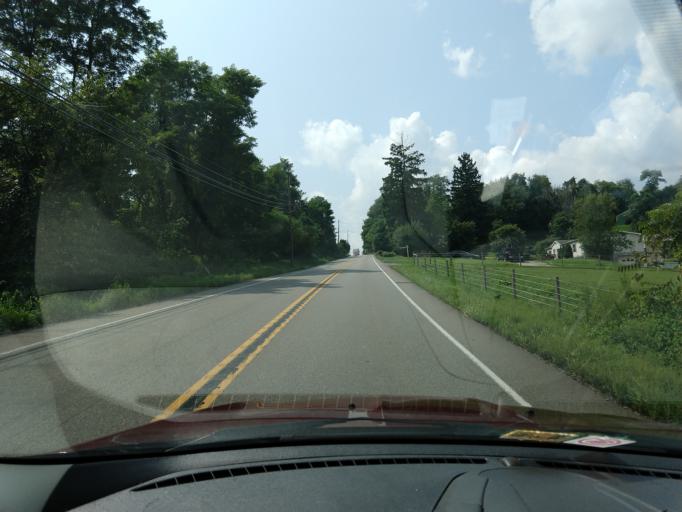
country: US
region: Pennsylvania
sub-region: Washington County
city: Baidland
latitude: 40.1959
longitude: -80.0057
